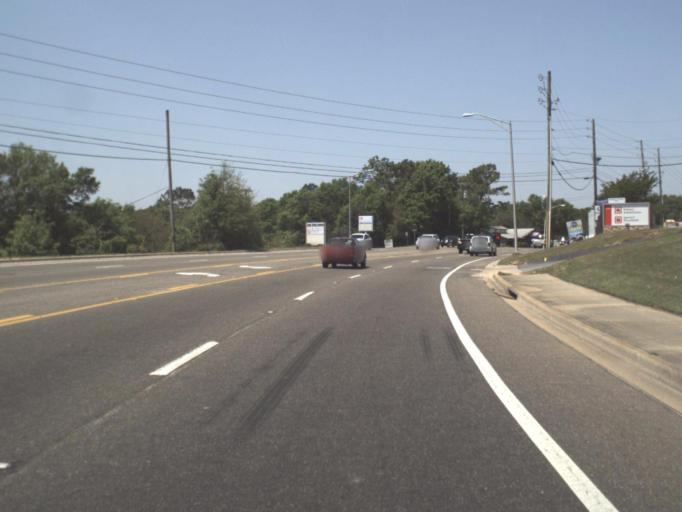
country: US
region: Florida
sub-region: Escambia County
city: Brent
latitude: 30.4801
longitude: -87.2174
